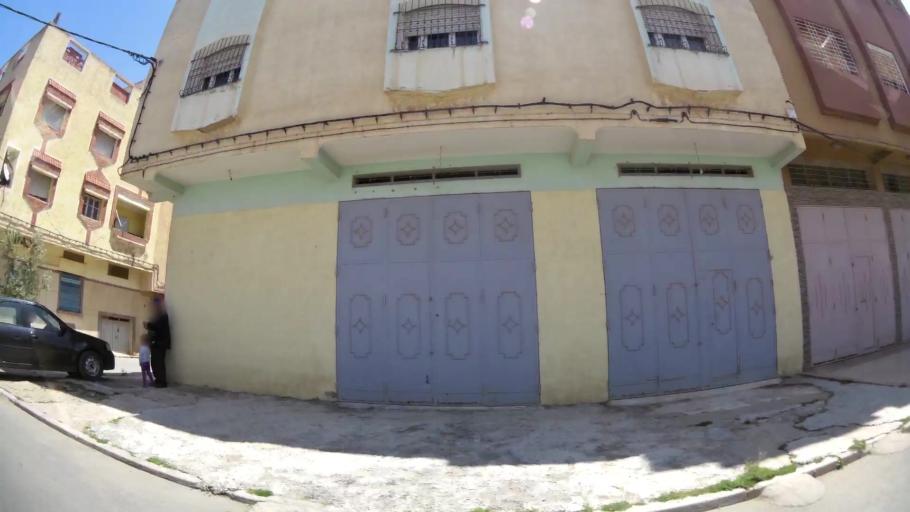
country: MA
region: Oriental
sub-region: Oujda-Angad
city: Oujda
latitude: 34.6965
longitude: -1.8960
